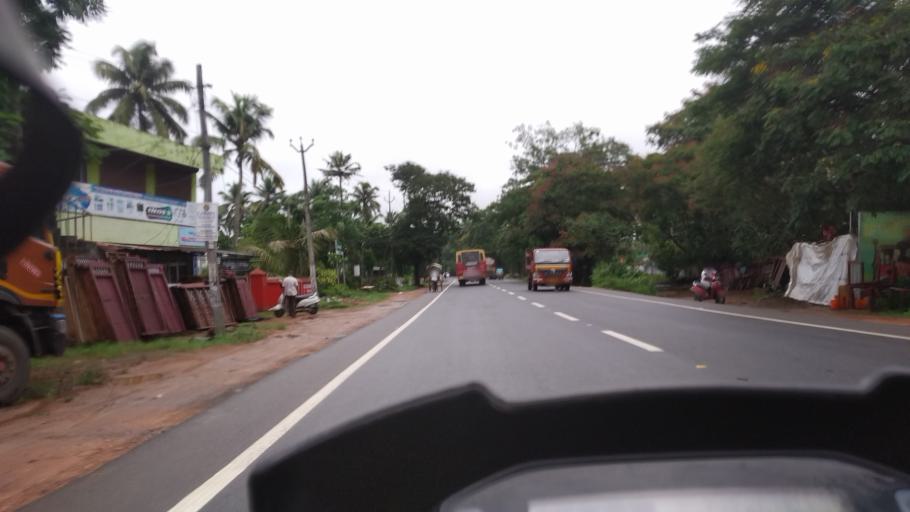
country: IN
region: Kerala
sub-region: Alappuzha
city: Mavelikara
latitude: 9.2860
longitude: 76.4394
